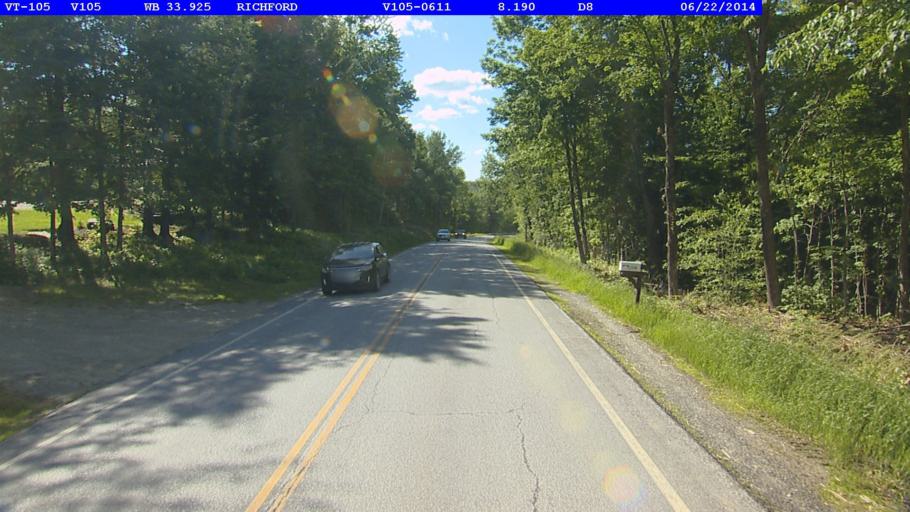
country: US
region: Vermont
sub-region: Franklin County
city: Richford
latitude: 44.9936
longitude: -72.5676
